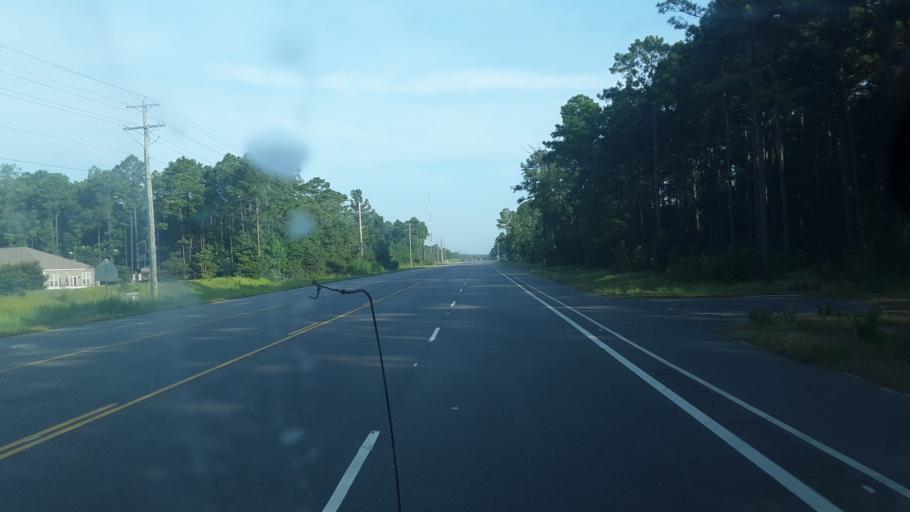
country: US
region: South Carolina
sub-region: Horry County
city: Myrtle Beach
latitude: 33.7697
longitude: -78.8677
